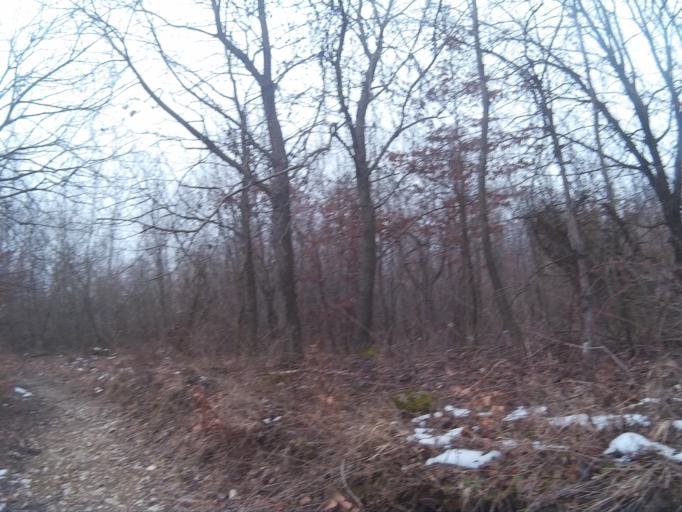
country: HU
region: Komarom-Esztergom
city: Tardos
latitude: 47.6771
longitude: 18.4699
